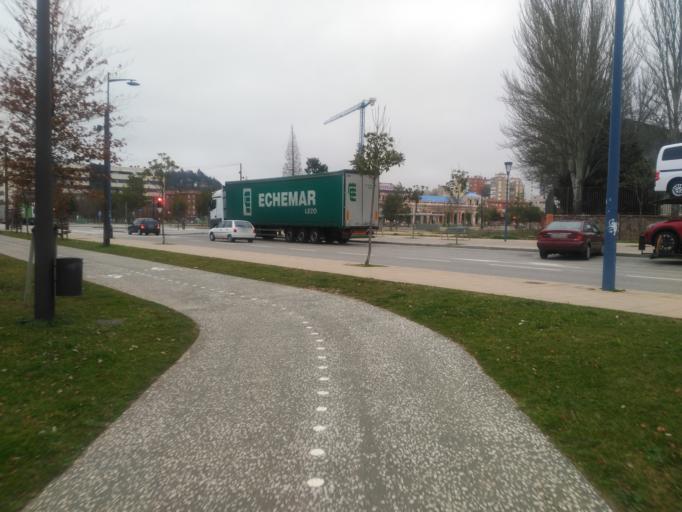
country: ES
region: Castille and Leon
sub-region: Provincia de Burgos
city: Burgos
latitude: 42.3329
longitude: -3.7089
